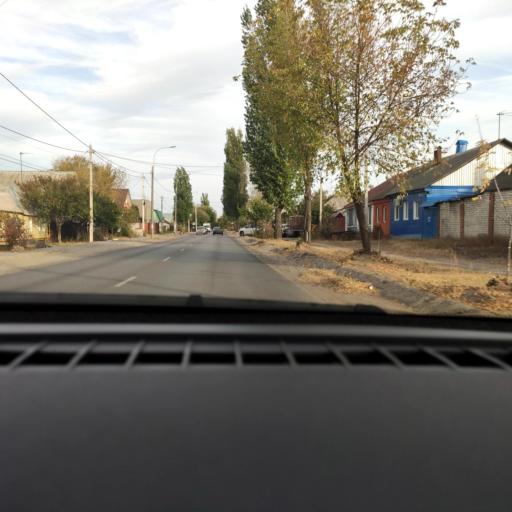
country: RU
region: Voronezj
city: Somovo
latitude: 51.7390
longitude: 39.2829
